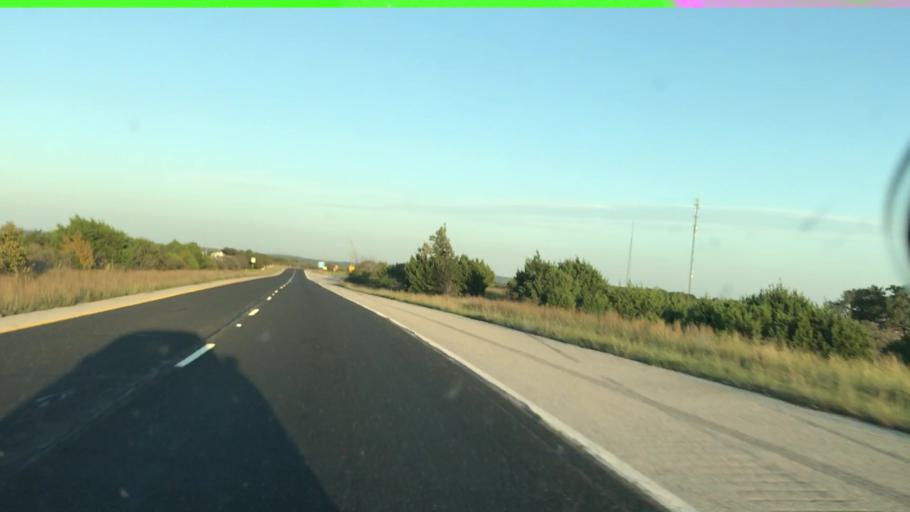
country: US
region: Texas
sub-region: Kerr County
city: Kerrville
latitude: 30.0534
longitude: -99.0326
